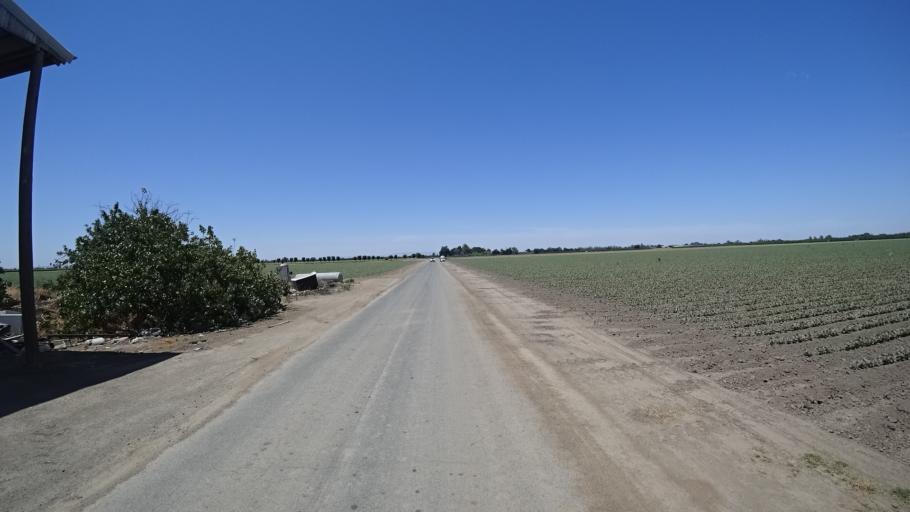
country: US
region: California
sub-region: Kings County
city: Lemoore
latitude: 36.3499
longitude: -119.7864
